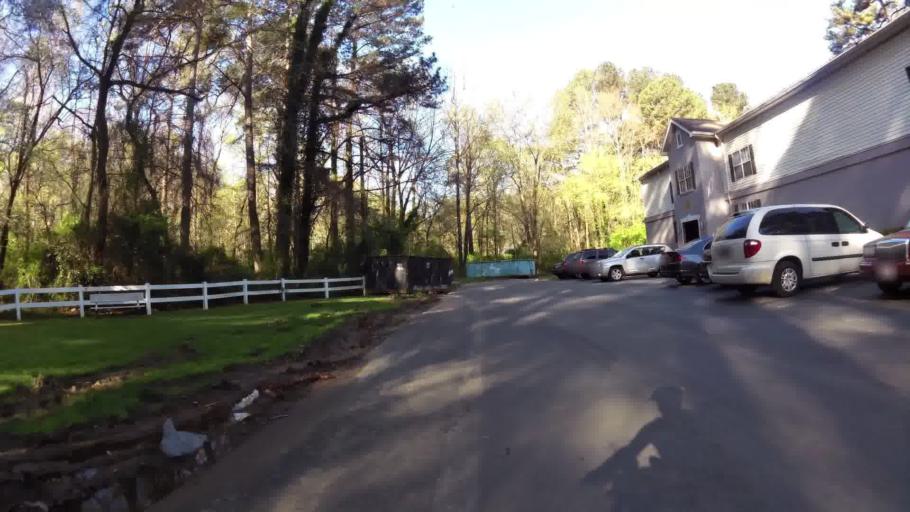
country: US
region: Georgia
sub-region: DeKalb County
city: Clarkston
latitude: 33.8365
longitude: -84.2615
